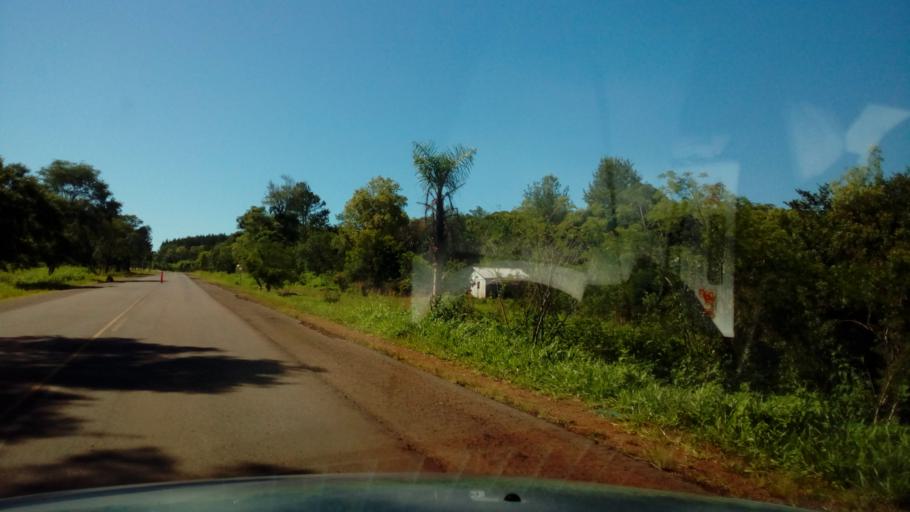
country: AR
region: Misiones
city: Almafuerte
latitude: -27.5553
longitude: -55.4208
